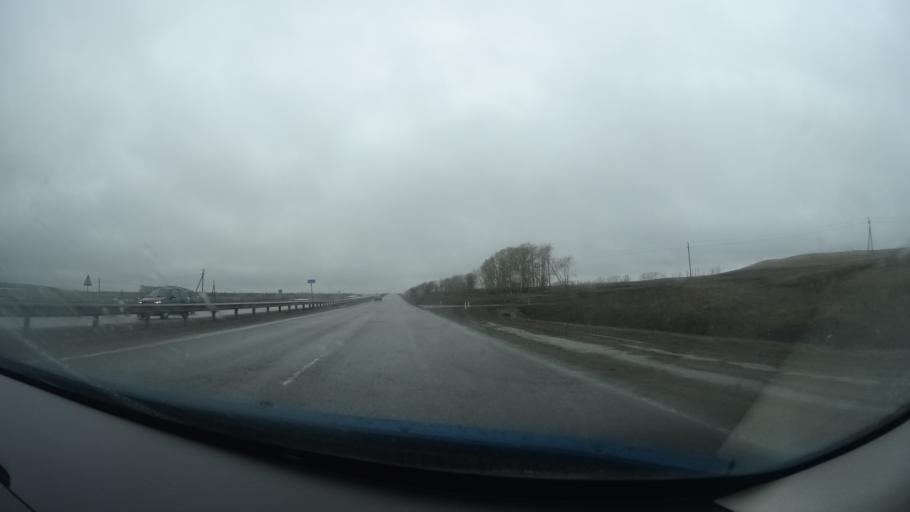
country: RU
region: Bashkortostan
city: Alekseyevka
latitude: 54.7280
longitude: 55.1498
